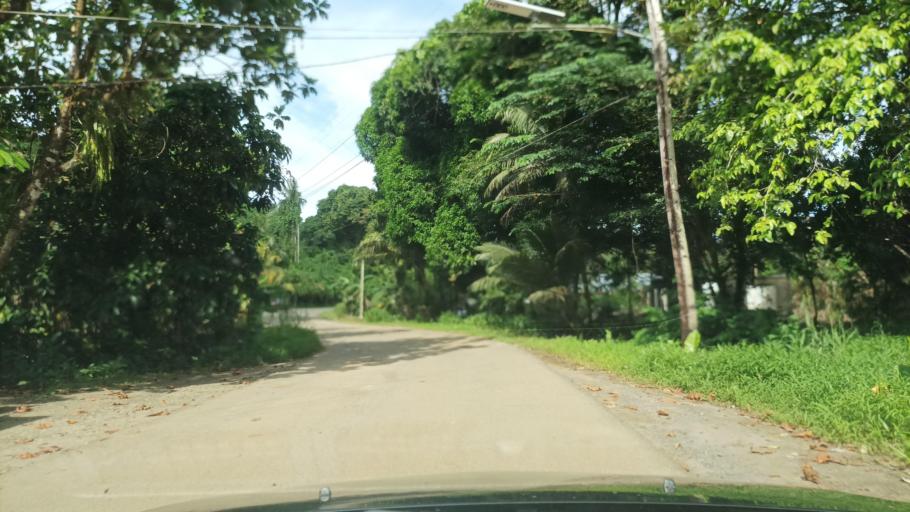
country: FM
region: Kosrae
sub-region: Lelu Municipality
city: Tofol
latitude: 5.3342
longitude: 163.0076
